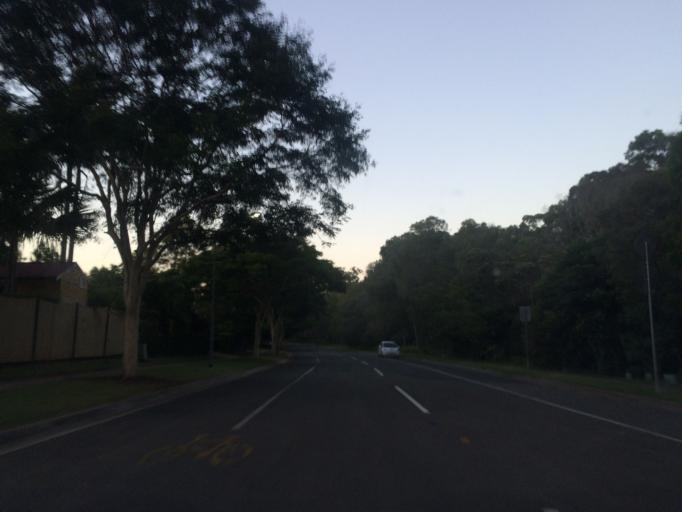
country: AU
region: Queensland
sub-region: Brisbane
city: Kenmore Hills
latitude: -27.4862
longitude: 152.9396
